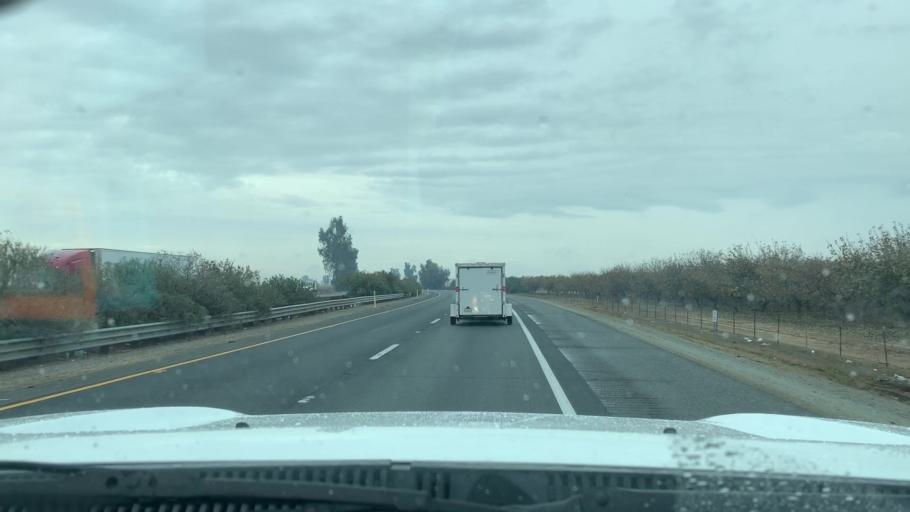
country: US
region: California
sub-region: Kern County
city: Delano
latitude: 35.8249
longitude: -119.2584
